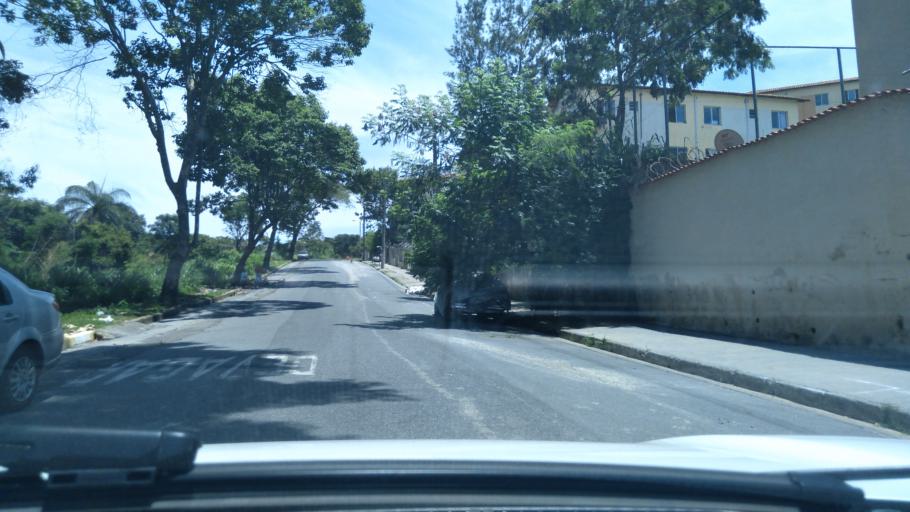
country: BR
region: Minas Gerais
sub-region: Contagem
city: Contagem
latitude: -19.9278
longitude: -44.0174
